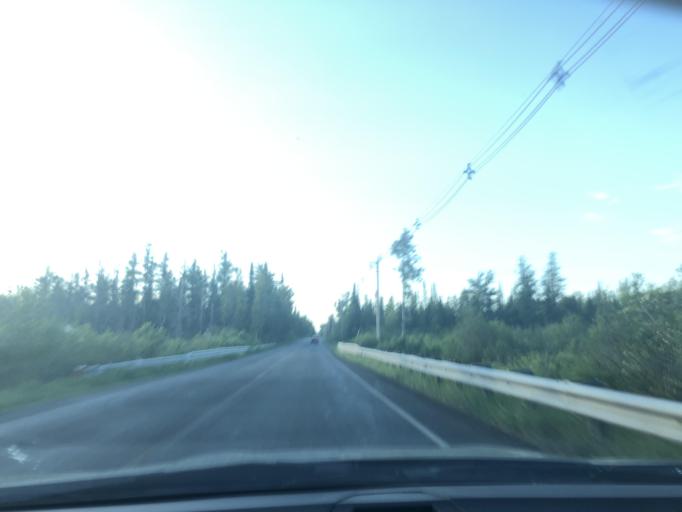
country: US
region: Michigan
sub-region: Missaukee County
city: Lake City
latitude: 44.3650
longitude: -85.0759
